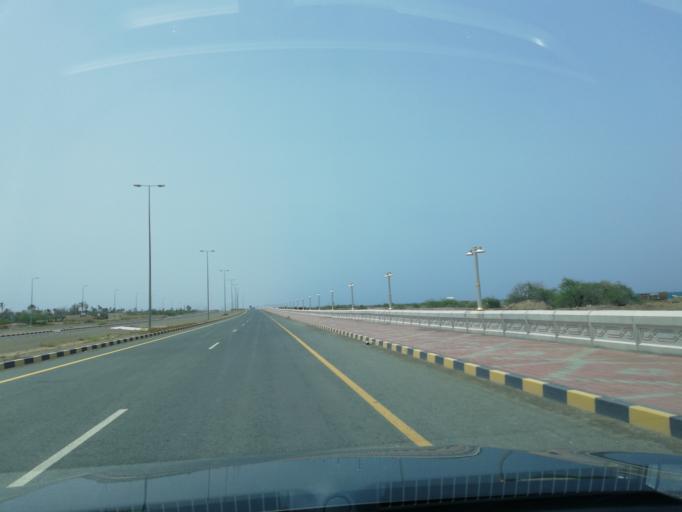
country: OM
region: Al Batinah
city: Al Liwa'
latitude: 24.6253
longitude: 56.5310
